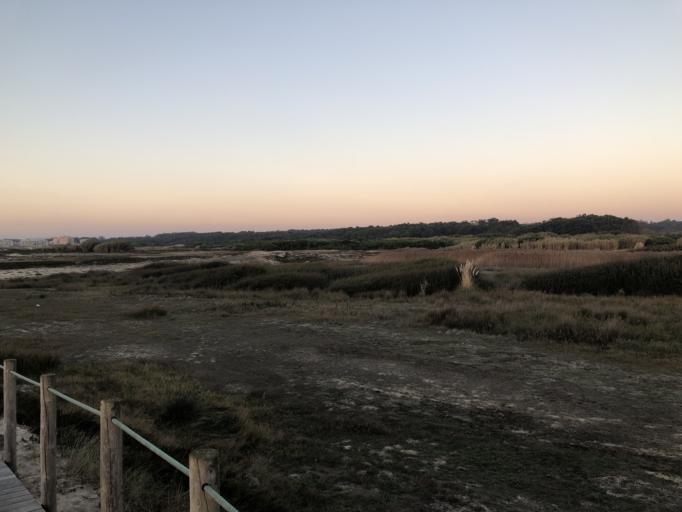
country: PT
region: Porto
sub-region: Vila do Conde
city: Arvore
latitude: 41.3156
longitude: -8.7390
